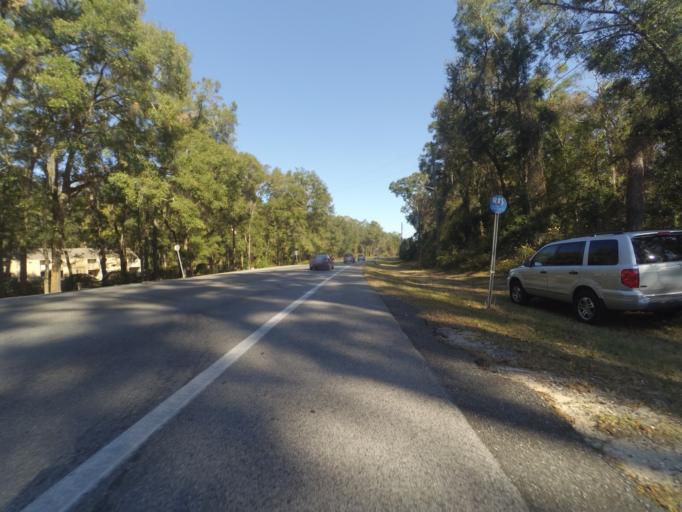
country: US
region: Florida
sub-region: Alachua County
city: Gainesville
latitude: 29.6392
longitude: -82.4108
